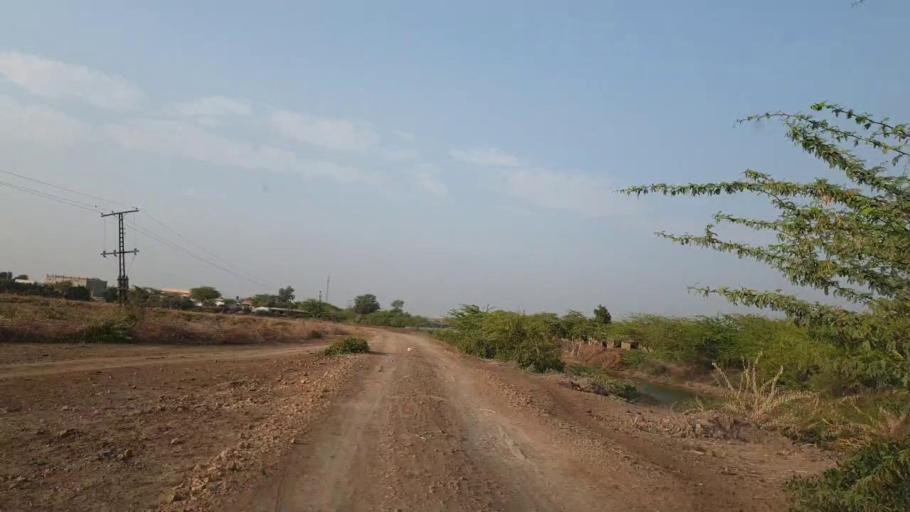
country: PK
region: Sindh
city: Pithoro
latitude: 25.5744
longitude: 69.3619
